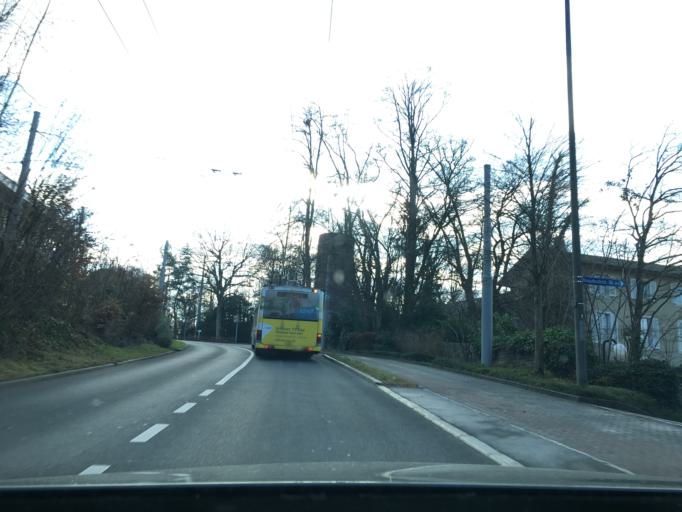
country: CH
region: Lucerne
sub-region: Lucerne-Land District
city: Adligenswil
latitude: 47.0515
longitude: 8.3435
